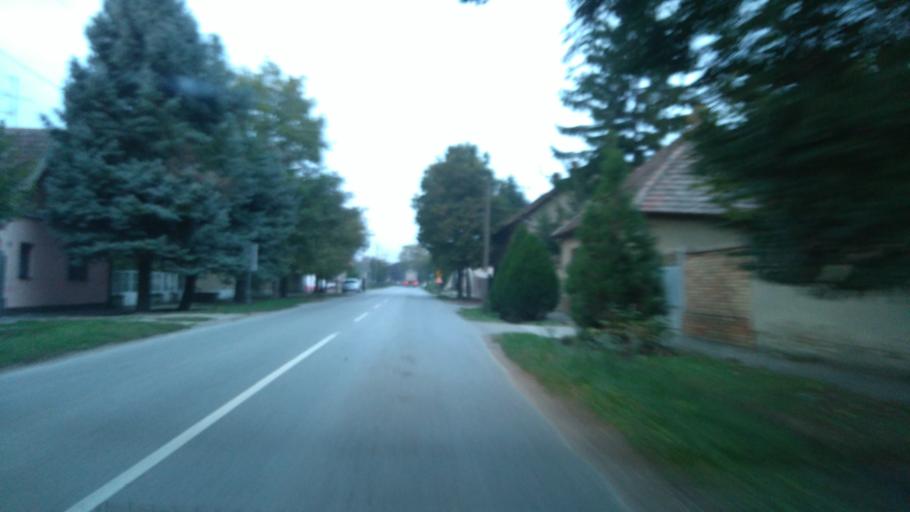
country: RS
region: Autonomna Pokrajina Vojvodina
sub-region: Severnobanatski Okrug
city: Ada
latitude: 45.7906
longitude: 20.1378
